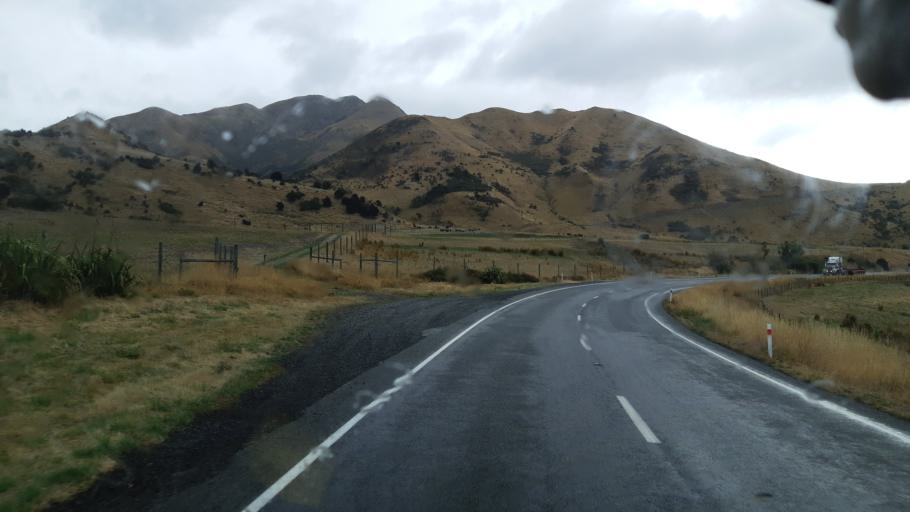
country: NZ
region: Canterbury
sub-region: Hurunui District
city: Amberley
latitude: -42.6416
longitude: 172.7719
